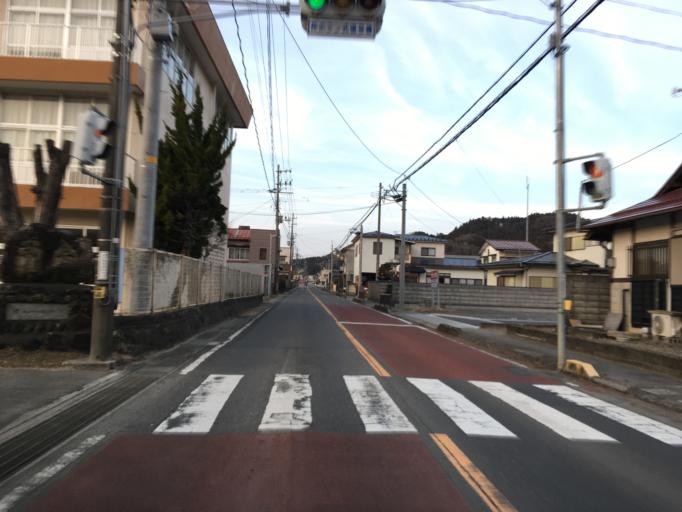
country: JP
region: Fukushima
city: Ishikawa
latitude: 36.9986
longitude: 140.3922
